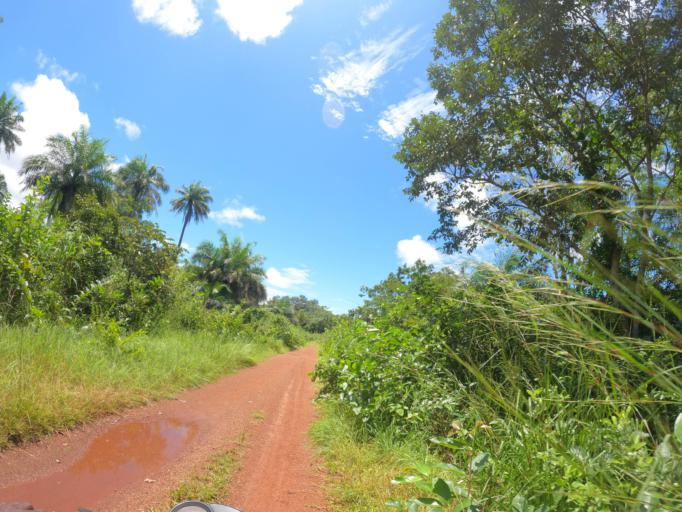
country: SL
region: Northern Province
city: Makeni
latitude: 9.0789
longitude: -12.2711
